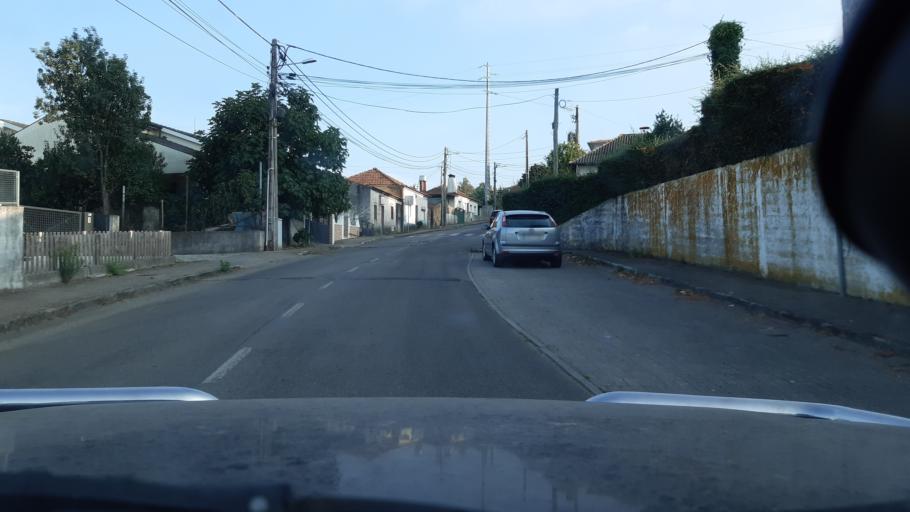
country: PT
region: Aveiro
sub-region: Agueda
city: Agueda
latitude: 40.5576
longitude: -8.4345
